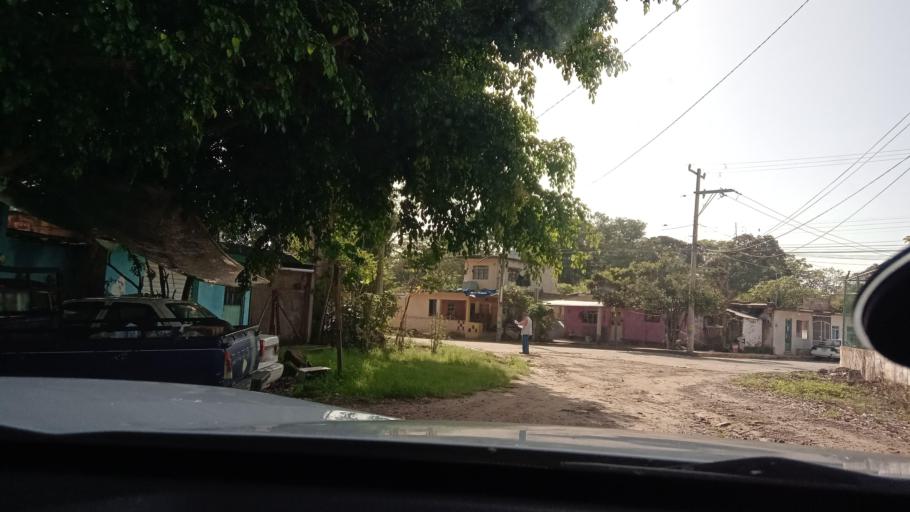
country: MX
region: Veracruz
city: El Castillo
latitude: 19.5662
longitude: -96.8642
